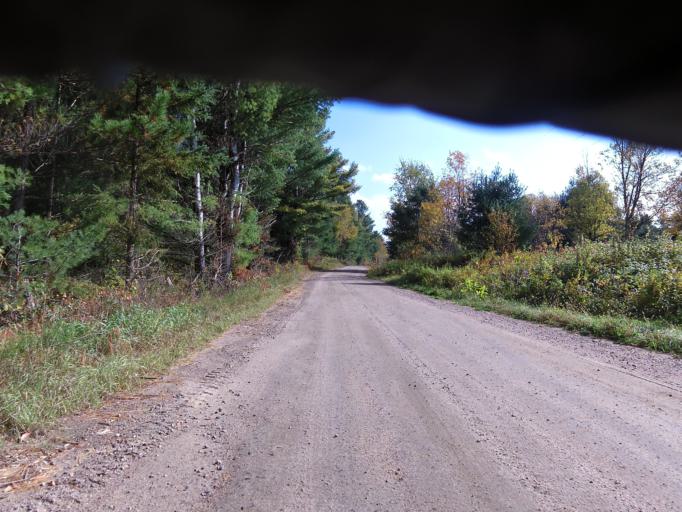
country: CA
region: Ontario
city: Petawawa
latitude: 45.8032
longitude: -77.3231
